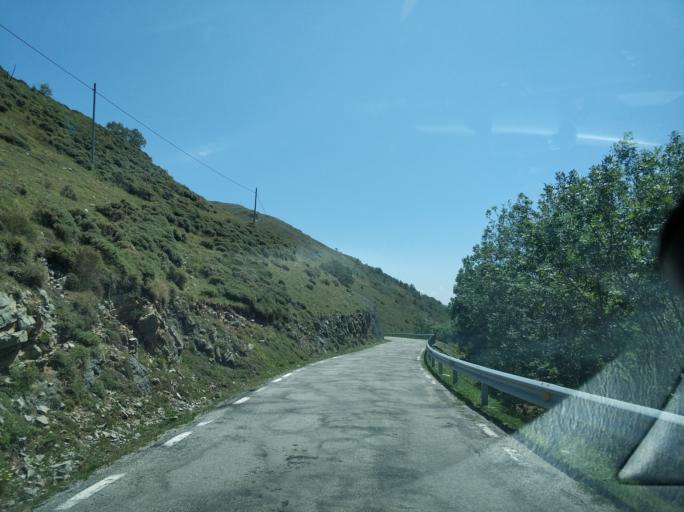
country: ES
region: Cantabria
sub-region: Provincia de Cantabria
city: Reinosa
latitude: 43.0309
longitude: -4.1707
